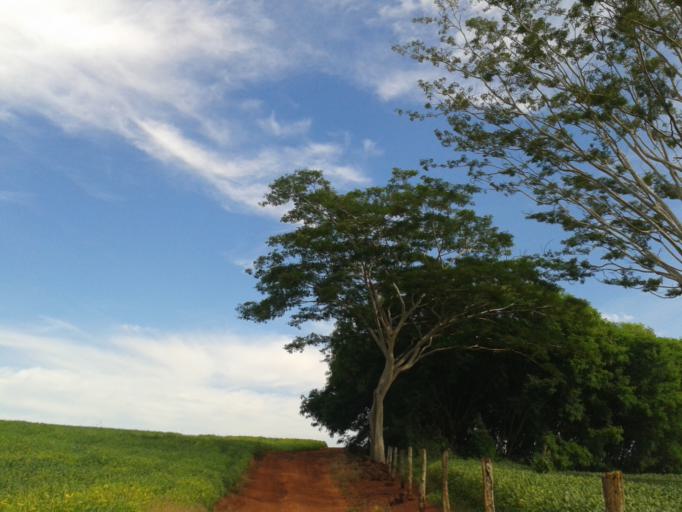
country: BR
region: Minas Gerais
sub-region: Capinopolis
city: Capinopolis
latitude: -18.6432
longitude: -49.7154
